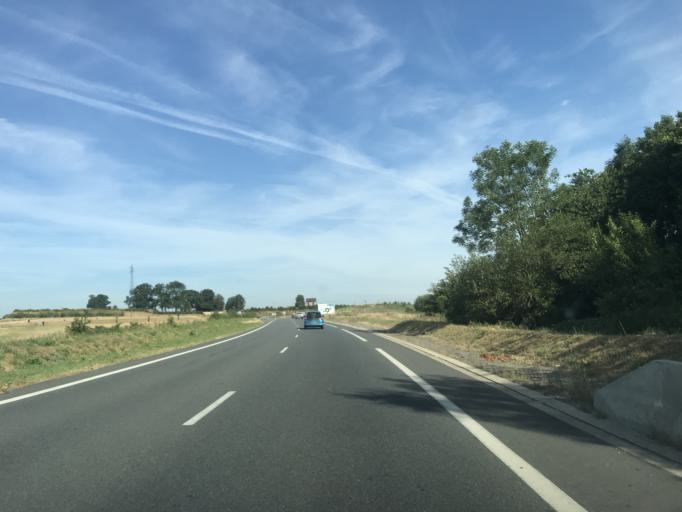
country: FR
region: Haute-Normandie
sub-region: Departement de la Seine-Maritime
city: Roumare
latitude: 49.5251
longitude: 0.9656
